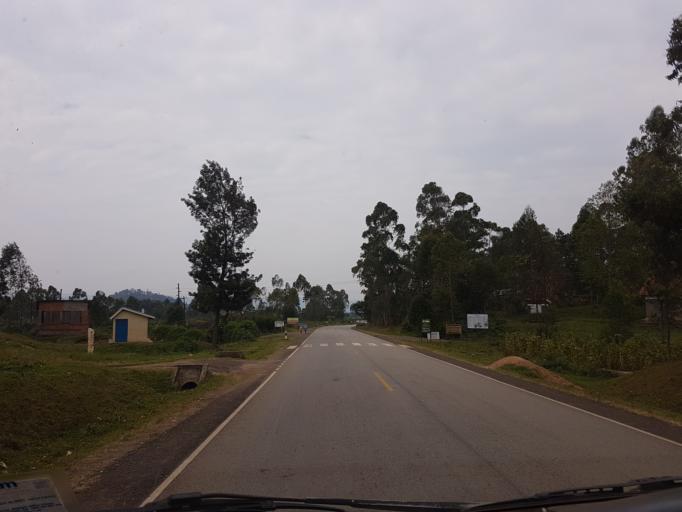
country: UG
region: Western Region
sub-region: Kisoro District
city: Kisoro
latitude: -1.3141
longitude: 29.7228
